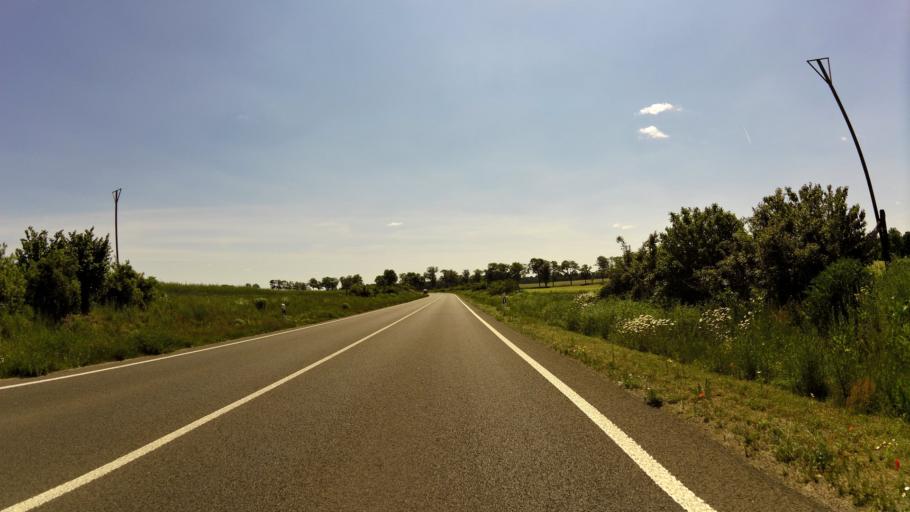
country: DE
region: Brandenburg
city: Rehfelde
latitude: 52.4842
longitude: 13.8789
